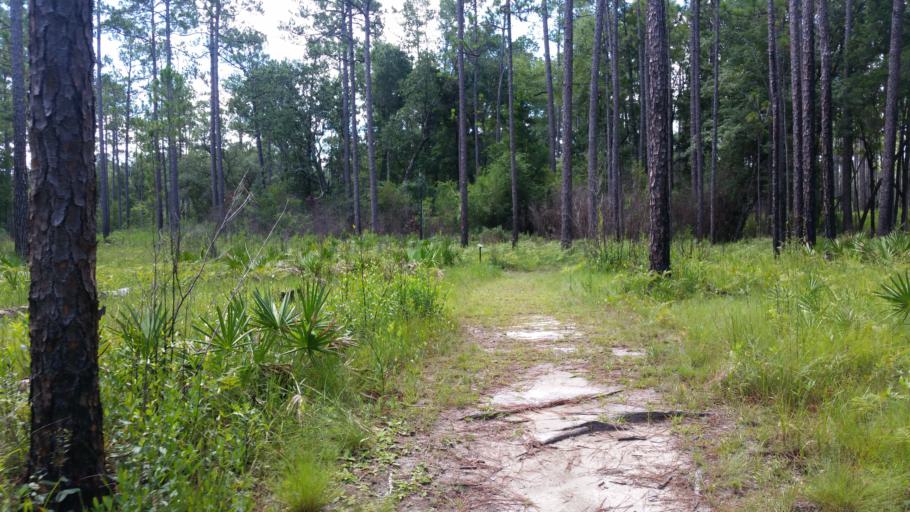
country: US
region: Florida
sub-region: Santa Rosa County
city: East Milton
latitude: 30.7067
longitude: -86.8724
